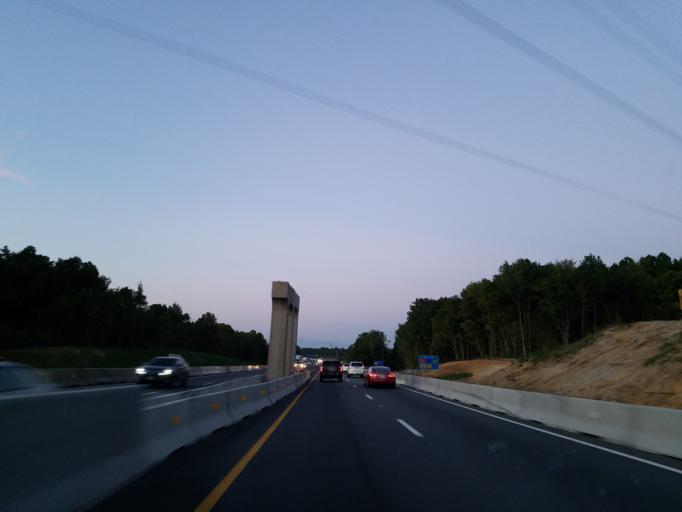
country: US
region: North Carolina
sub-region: Cabarrus County
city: Kannapolis
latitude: 35.4907
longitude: -80.5699
